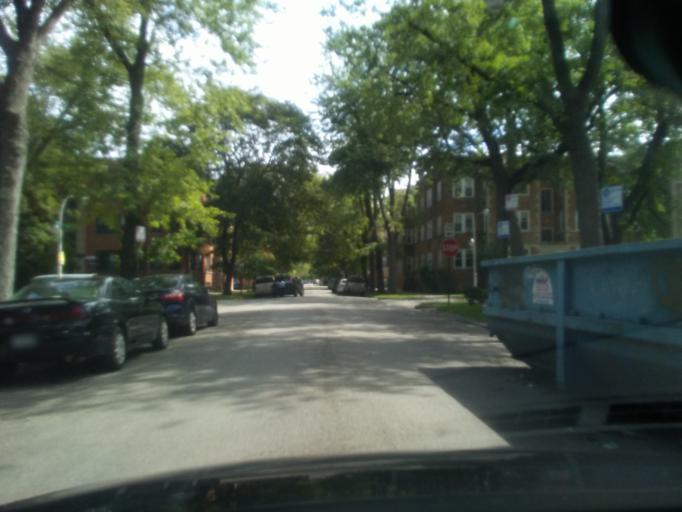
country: US
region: Illinois
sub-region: Cook County
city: Lincolnwood
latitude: 41.9957
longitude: -87.7025
